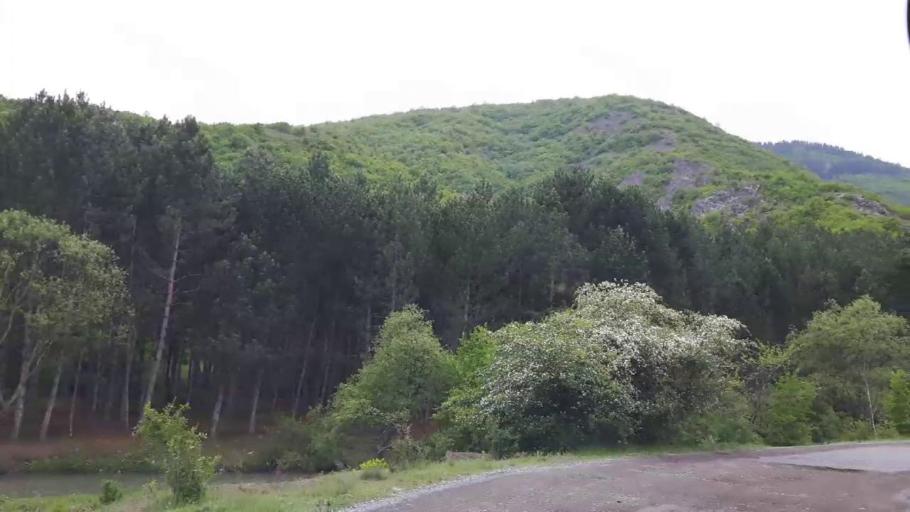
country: GE
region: Shida Kartli
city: Gori
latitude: 41.8965
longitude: 44.0452
